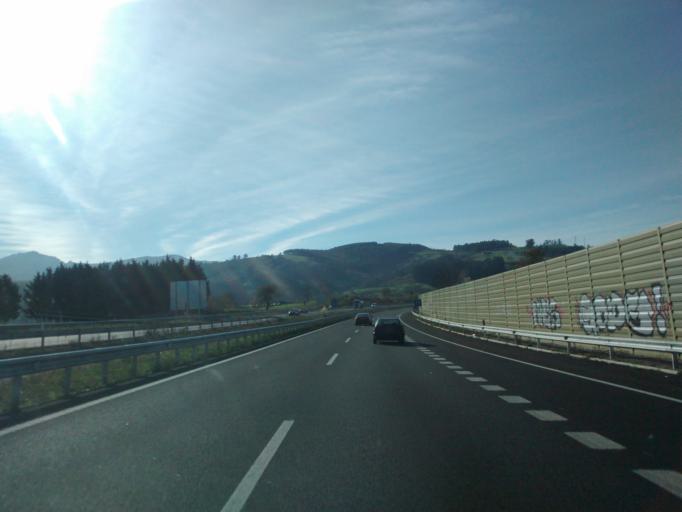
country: ES
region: Cantabria
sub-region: Provincia de Cantabria
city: Lierganes
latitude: 43.3632
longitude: -3.7598
